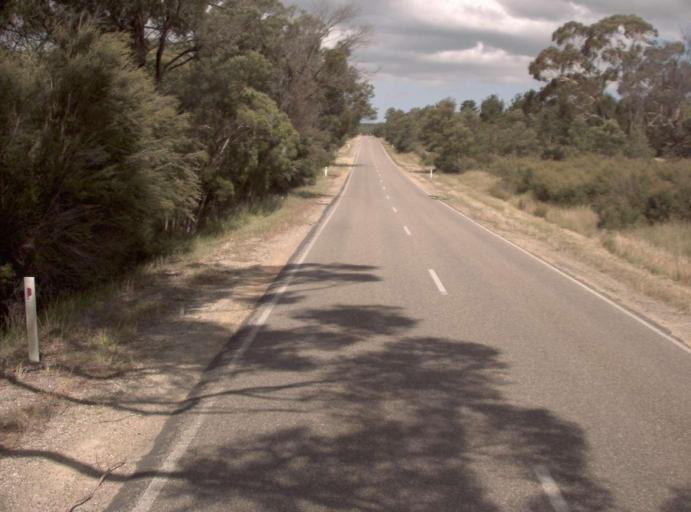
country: AU
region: Victoria
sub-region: Wellington
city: Sale
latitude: -38.1676
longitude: 146.9581
